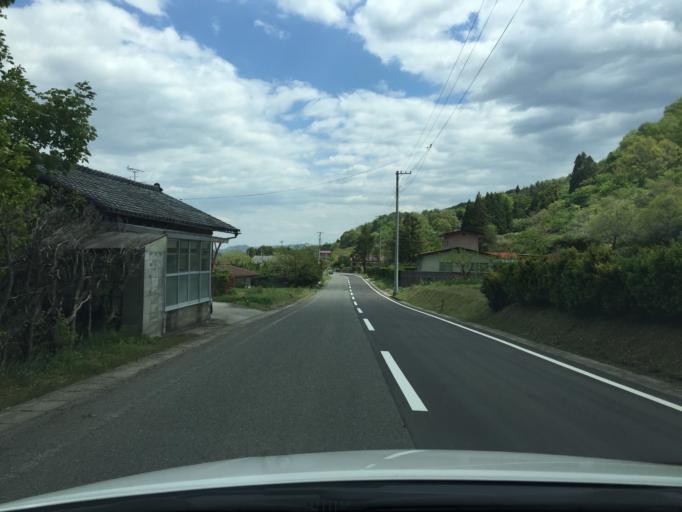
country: JP
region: Fukushima
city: Hobaramachi
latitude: 37.7396
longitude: 140.5597
